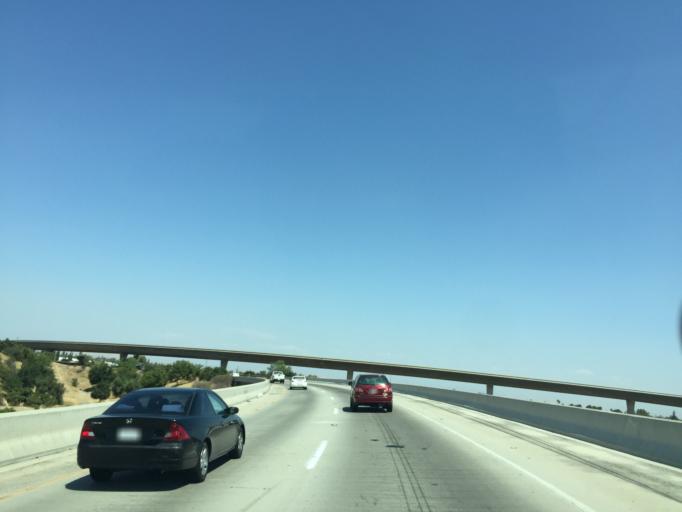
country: US
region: California
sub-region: Fresno County
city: Fresno
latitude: 36.7550
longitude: -119.7509
